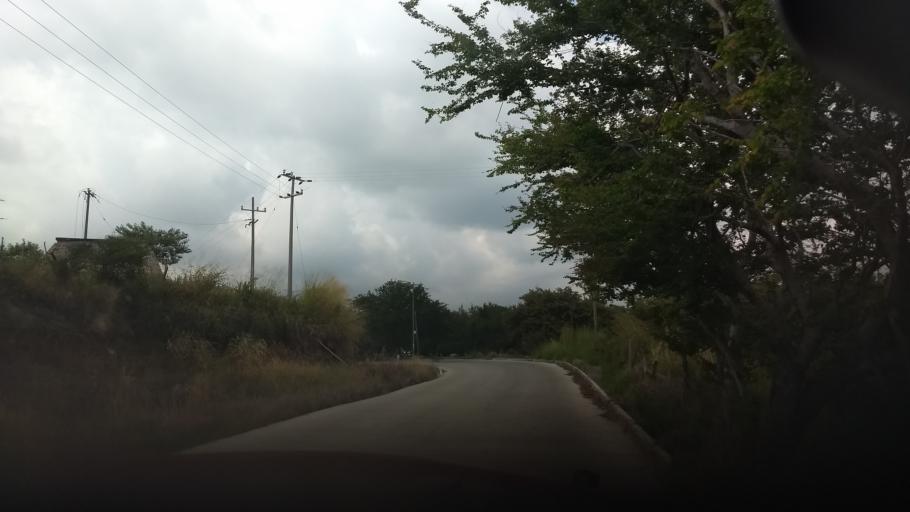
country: MX
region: Jalisco
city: Tonila
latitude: 19.3953
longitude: -103.5298
